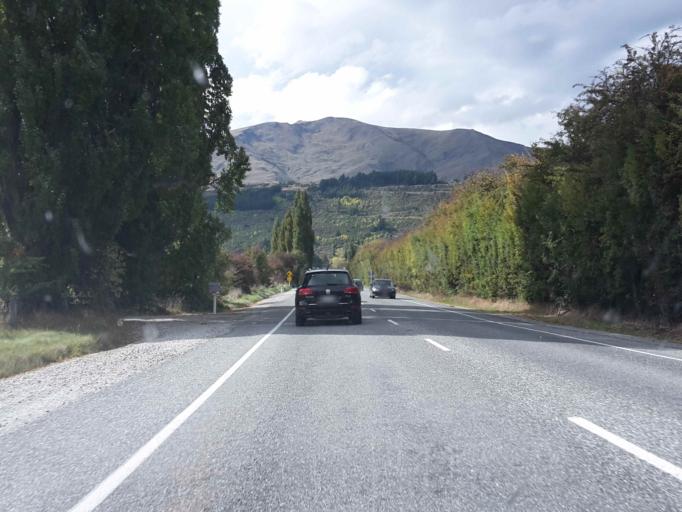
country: NZ
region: Otago
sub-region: Queenstown-Lakes District
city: Arrowtown
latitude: -44.9816
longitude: 168.8392
